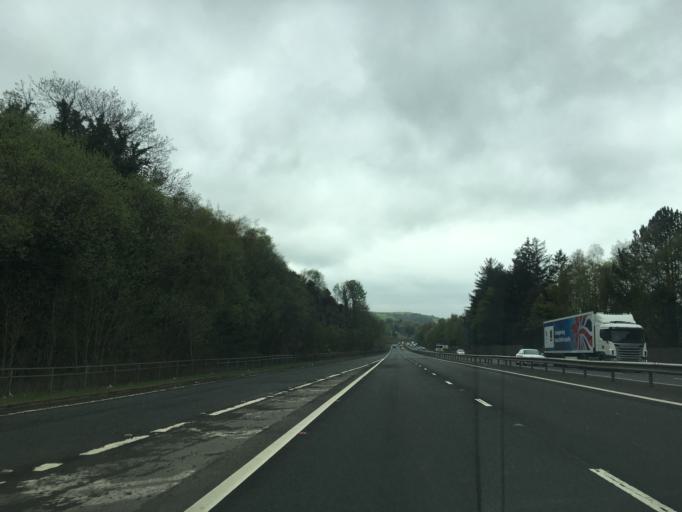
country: GB
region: Scotland
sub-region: West Dunbartonshire
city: Dumbarton
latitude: 55.9234
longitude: -4.5603
